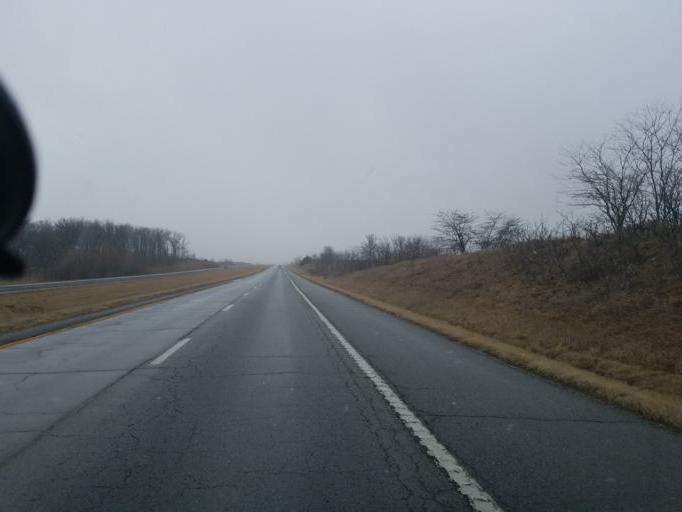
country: US
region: Missouri
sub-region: Macon County
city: La Plata
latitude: 39.9938
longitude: -92.4757
